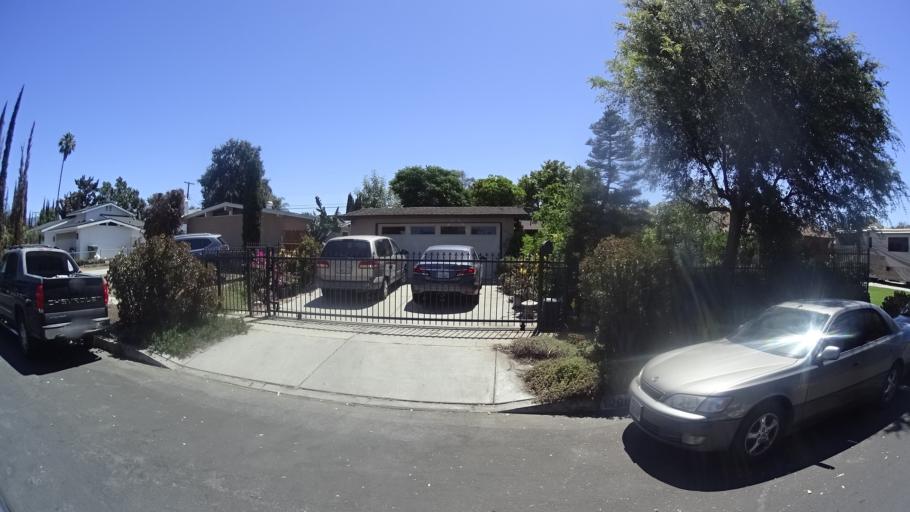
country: US
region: California
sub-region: Los Angeles County
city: San Fernando
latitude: 34.2520
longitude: -118.4565
